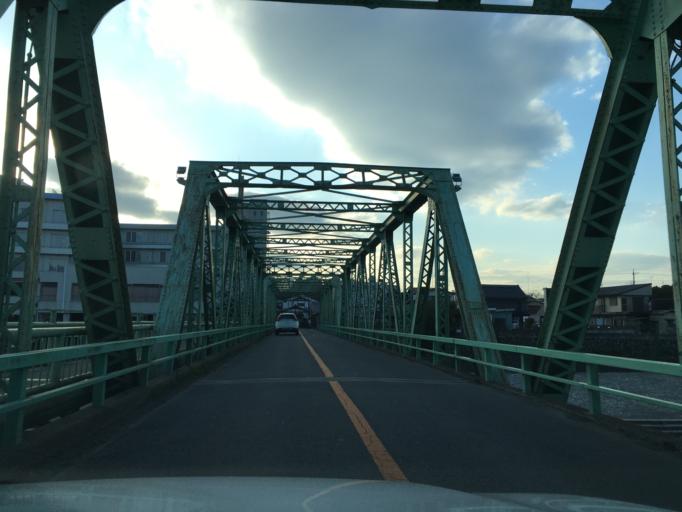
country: JP
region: Tochigi
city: Otawara
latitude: 36.8589
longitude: 140.1185
